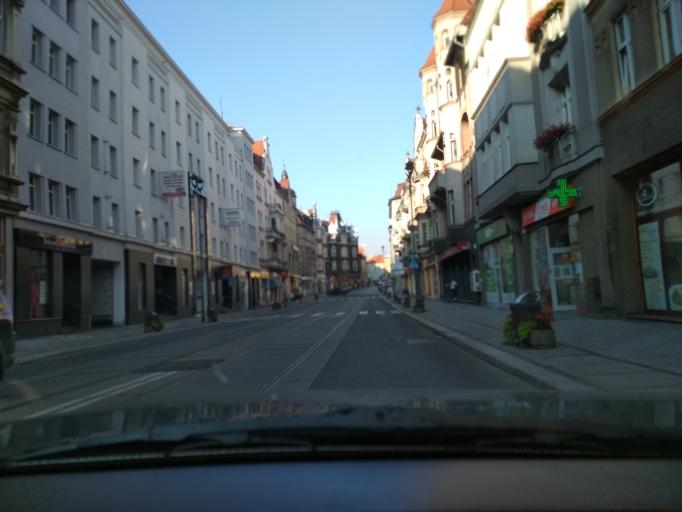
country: PL
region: Silesian Voivodeship
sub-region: Gliwice
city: Gliwice
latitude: 50.2955
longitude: 18.6689
